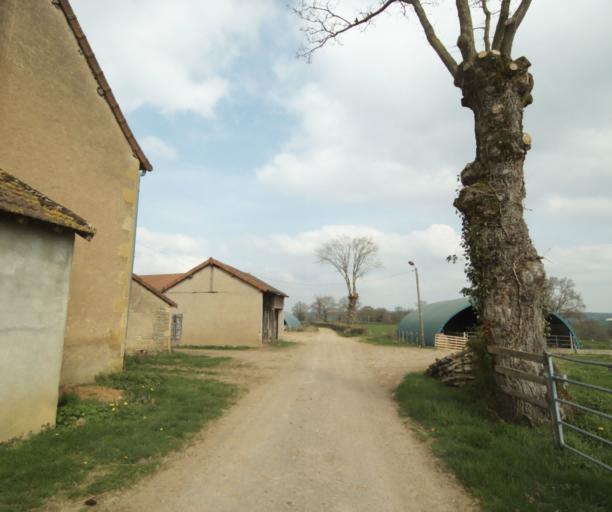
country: FR
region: Bourgogne
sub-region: Departement de Saone-et-Loire
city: Charolles
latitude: 46.4007
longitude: 4.2373
